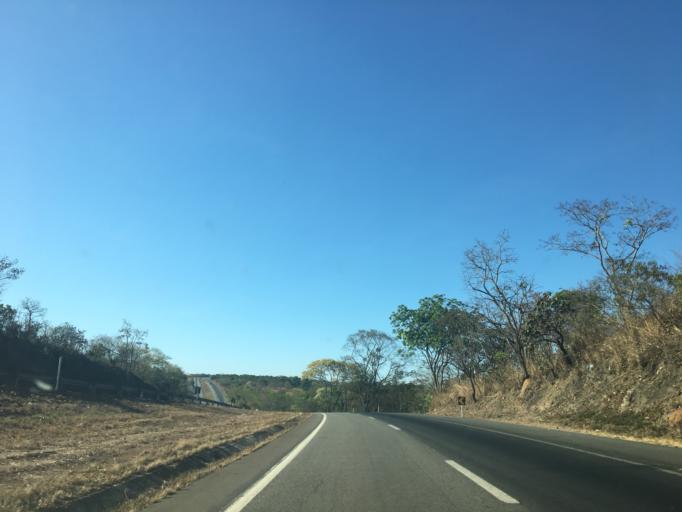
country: BR
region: Goias
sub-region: Hidrolandia
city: Hidrolandia
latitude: -17.0772
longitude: -49.2232
